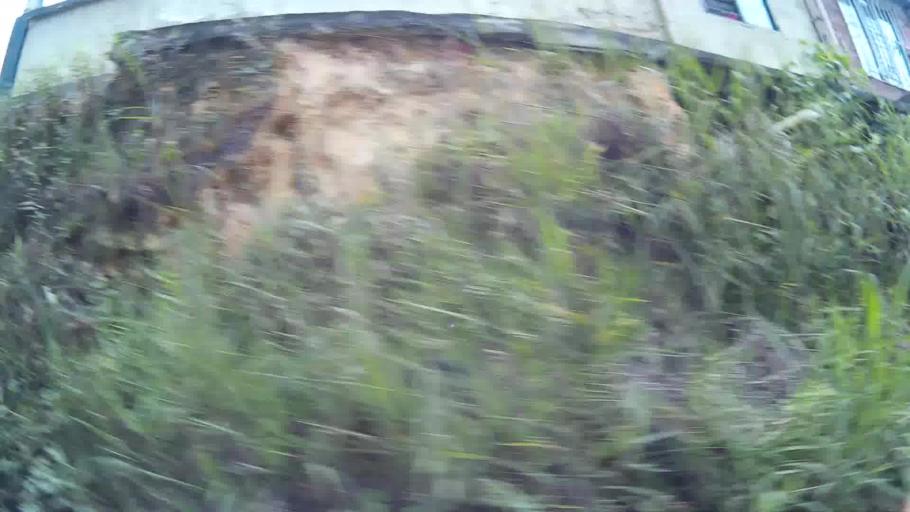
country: CO
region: Antioquia
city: Medellin
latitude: 6.2658
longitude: -75.6271
